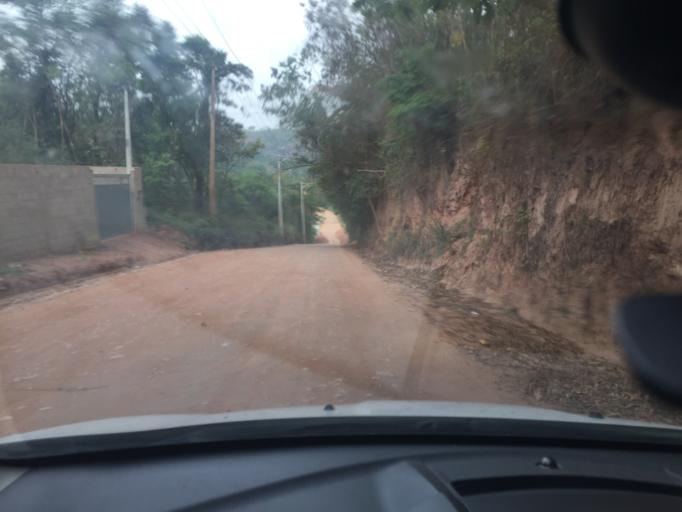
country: BR
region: Sao Paulo
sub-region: Campo Limpo Paulista
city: Campo Limpo Paulista
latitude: -23.1903
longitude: -46.7918
